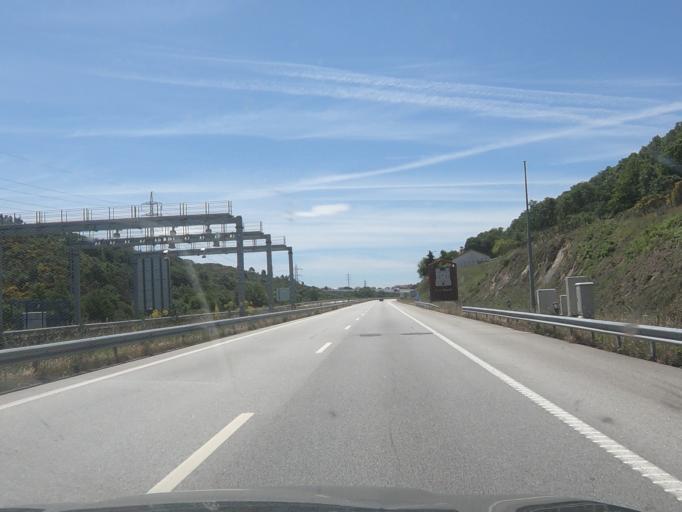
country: PT
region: Guarda
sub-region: Guarda
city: Sequeira
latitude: 40.5776
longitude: -7.2517
